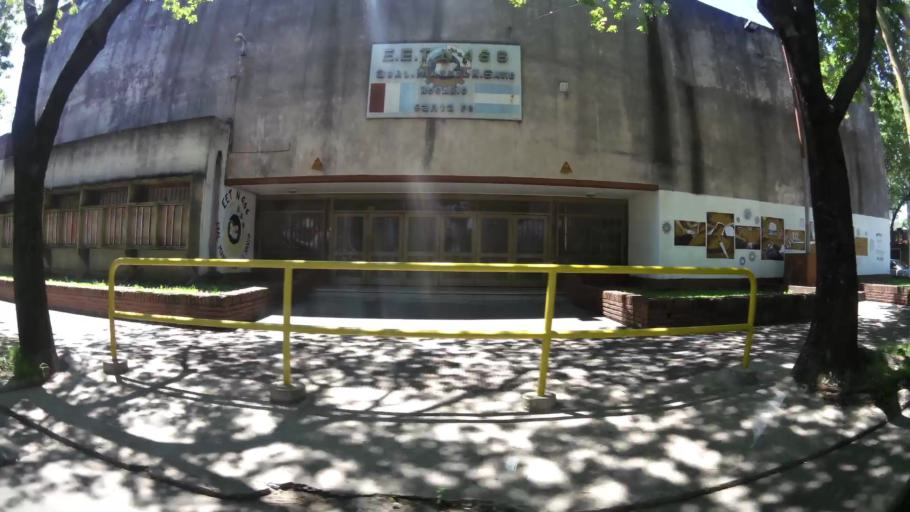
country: AR
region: Santa Fe
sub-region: Departamento de Rosario
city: Rosario
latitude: -32.9420
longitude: -60.7022
